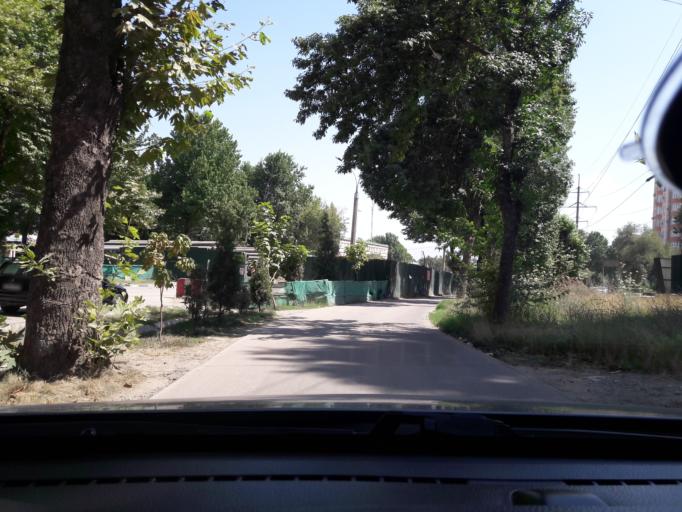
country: TJ
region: Dushanbe
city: Dushanbe
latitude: 38.5882
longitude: 68.7550
